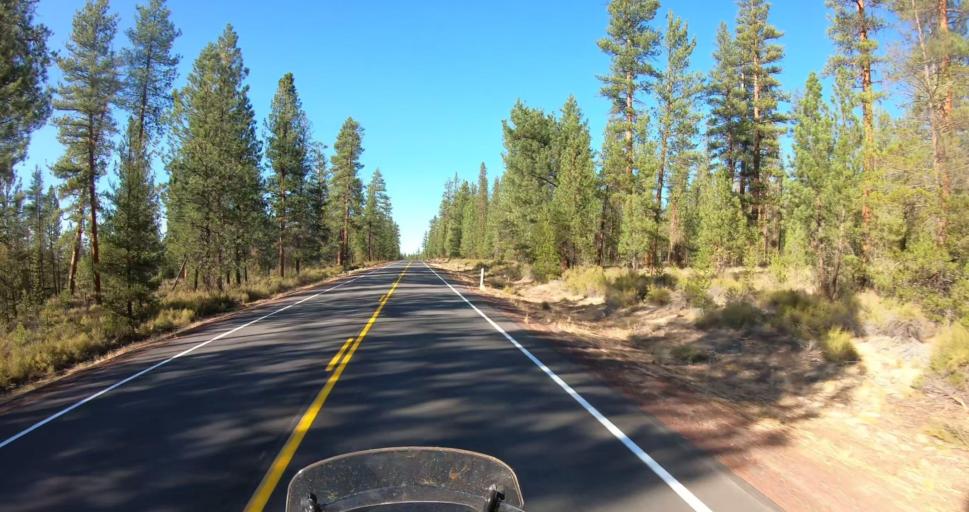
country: US
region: Oregon
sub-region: Deschutes County
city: La Pine
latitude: 43.5067
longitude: -121.4507
